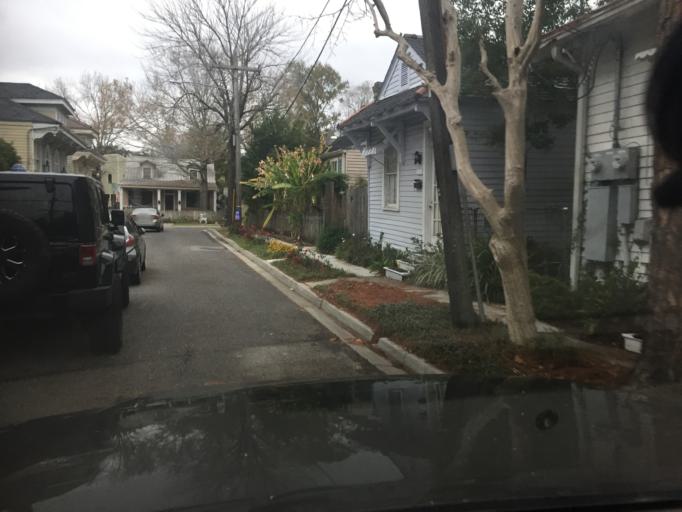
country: US
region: Louisiana
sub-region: Orleans Parish
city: New Orleans
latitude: 29.9801
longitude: -90.0862
